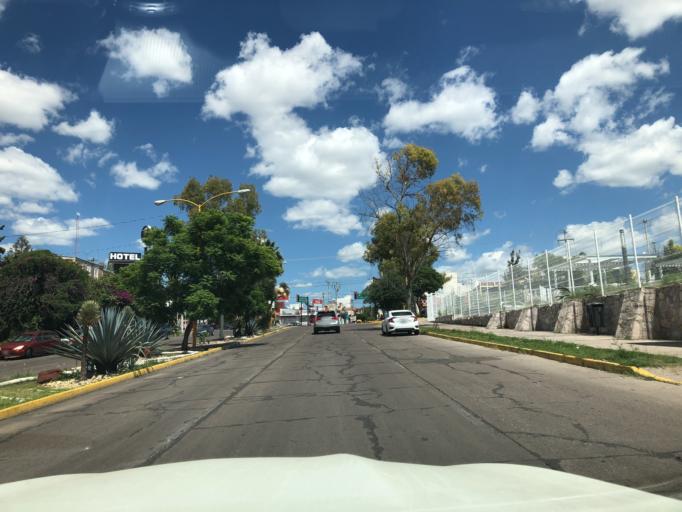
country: MX
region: Aguascalientes
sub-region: Aguascalientes
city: Aguascalientes
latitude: 21.8712
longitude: -102.3079
